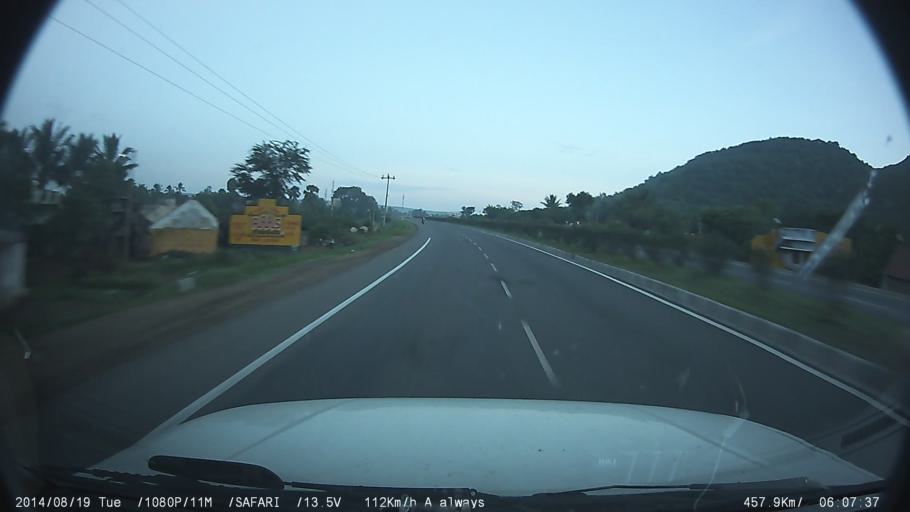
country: IN
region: Tamil Nadu
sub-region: Salem
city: Omalur
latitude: 11.9030
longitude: 78.0617
